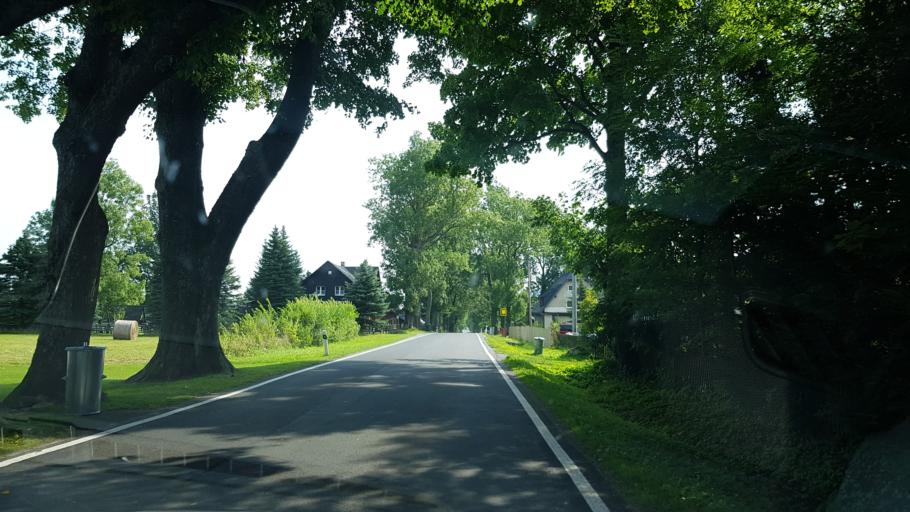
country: CZ
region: Olomoucky
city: Pisecna
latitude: 50.2296
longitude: 17.3010
